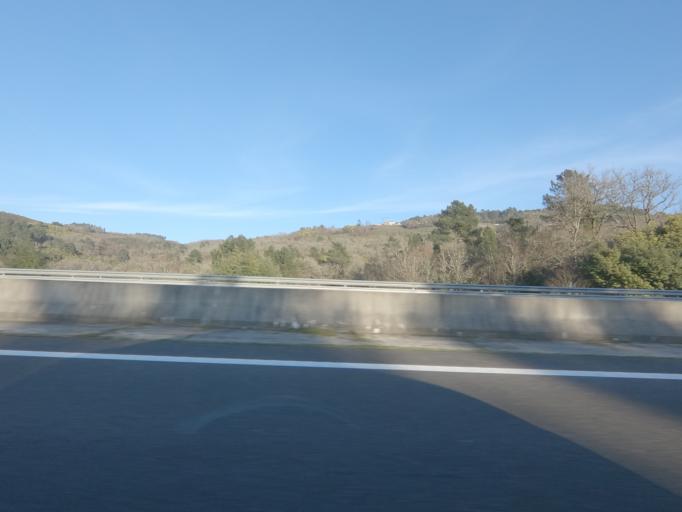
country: ES
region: Galicia
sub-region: Provincia de Ourense
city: Punxin
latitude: 42.3602
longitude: -7.9965
